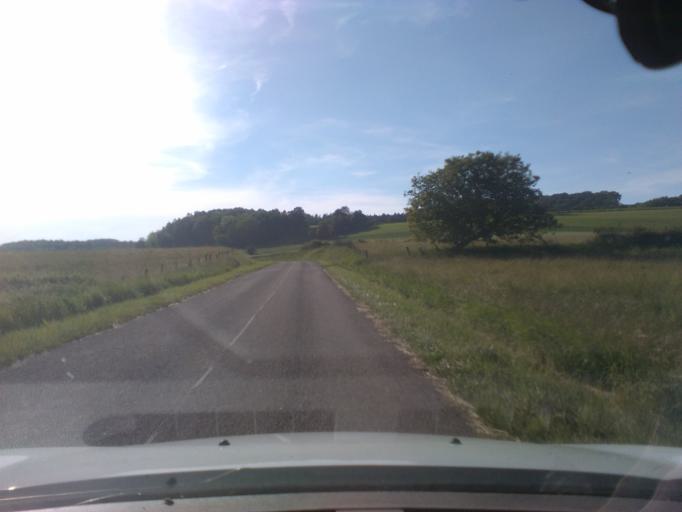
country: FR
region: Lorraine
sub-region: Departement des Vosges
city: Mirecourt
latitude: 48.2665
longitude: 6.2170
